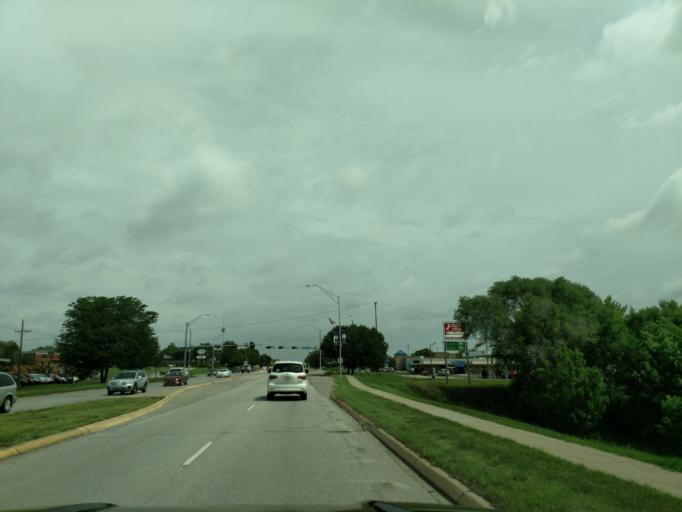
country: US
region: Nebraska
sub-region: Sarpy County
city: La Vista
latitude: 41.1864
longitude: -96.0429
